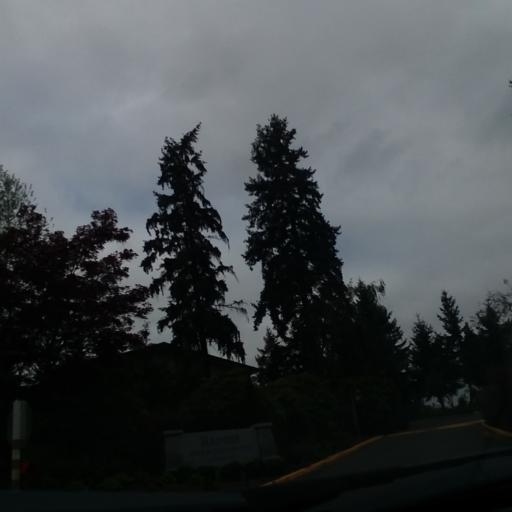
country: US
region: Washington
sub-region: King County
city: Boulevard Park
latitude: 47.5031
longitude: -122.3060
